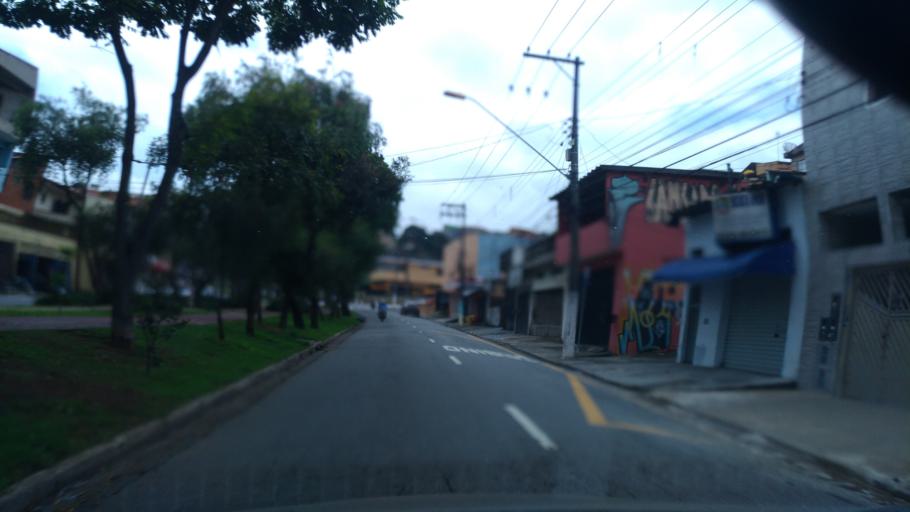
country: BR
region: Sao Paulo
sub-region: Santo Andre
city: Santo Andre
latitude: -23.6961
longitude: -46.5141
